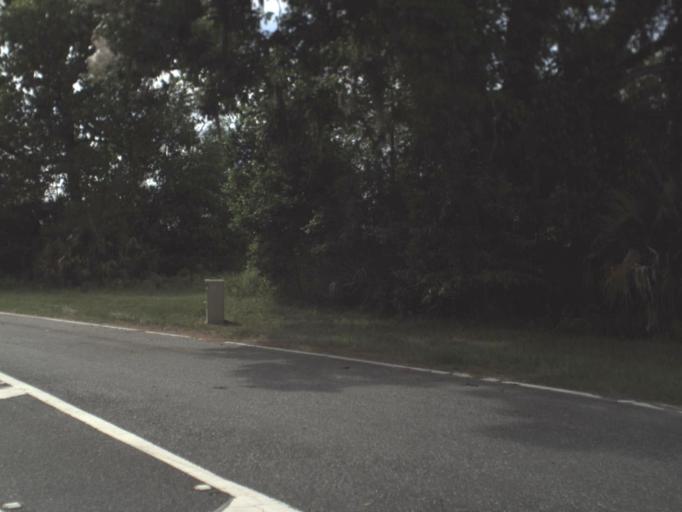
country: US
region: Florida
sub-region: Taylor County
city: Perry
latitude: 30.0811
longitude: -83.5087
